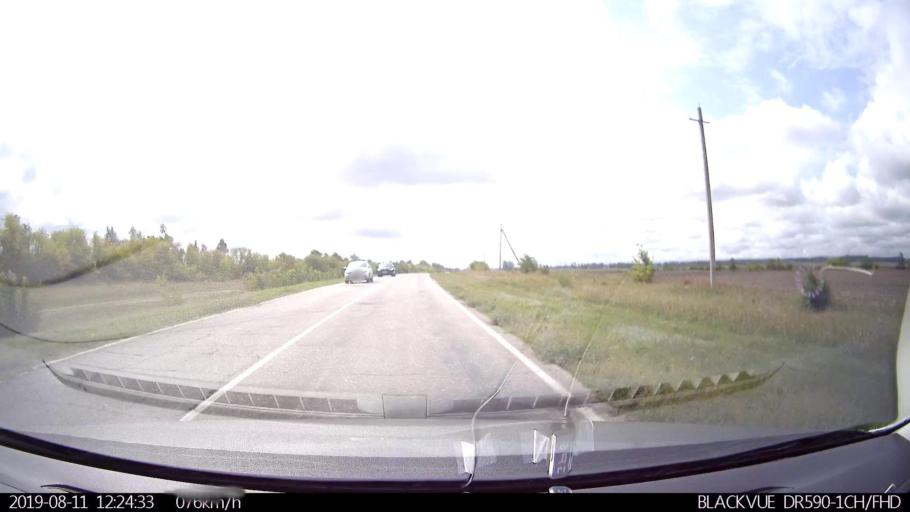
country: RU
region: Ulyanovsk
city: Ignatovka
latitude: 53.8820
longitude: 47.9477
